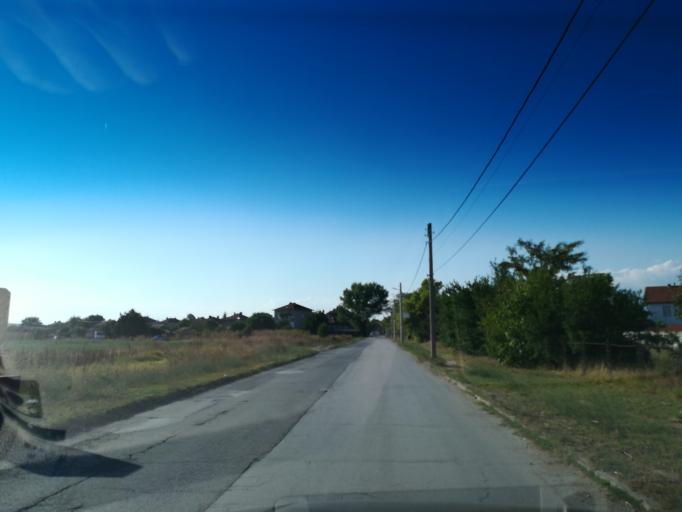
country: BG
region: Stara Zagora
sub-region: Obshtina Chirpan
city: Chirpan
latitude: 42.0935
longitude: 25.2352
